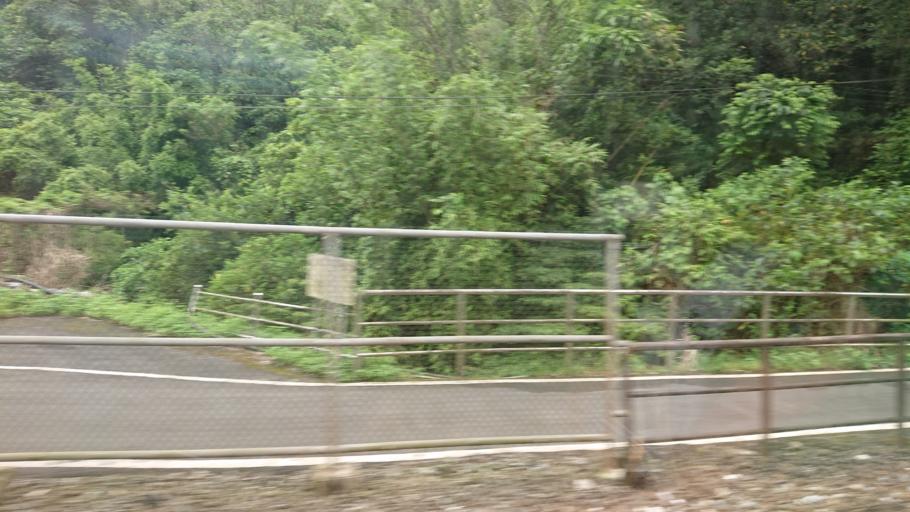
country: TW
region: Taiwan
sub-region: Keelung
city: Keelung
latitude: 25.0578
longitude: 121.8462
